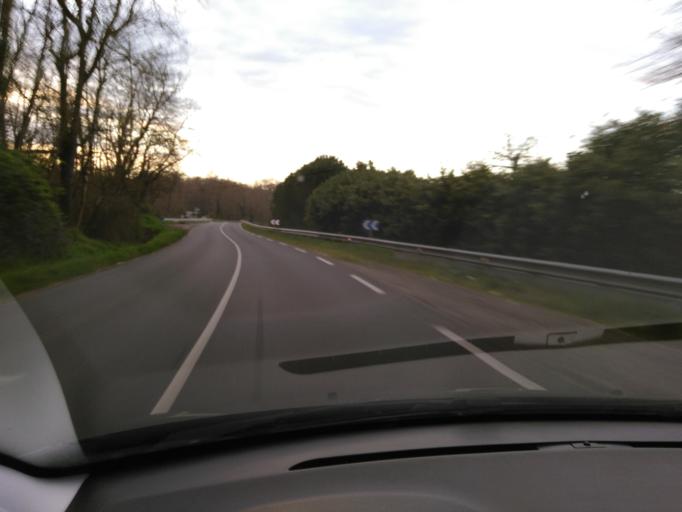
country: FR
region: Midi-Pyrenees
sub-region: Departement de la Haute-Garonne
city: Brax
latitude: 43.6156
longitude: 1.2599
